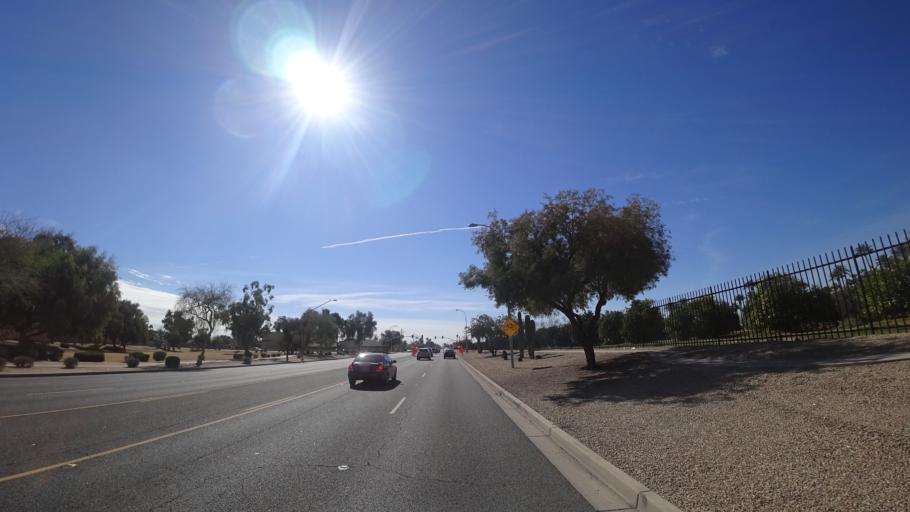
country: US
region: Arizona
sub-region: Maricopa County
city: Glendale
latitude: 33.5761
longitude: -112.1863
